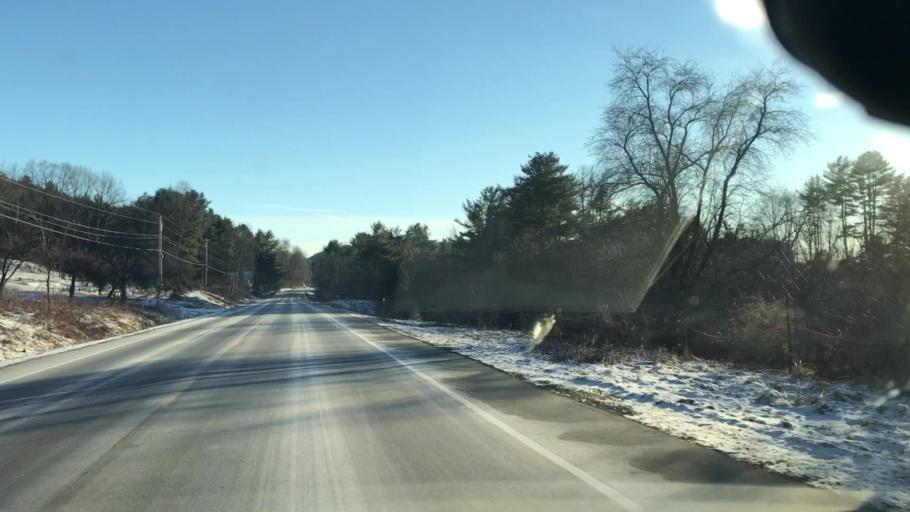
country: US
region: New Hampshire
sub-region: Grafton County
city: Lyme Town Offices
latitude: 43.8599
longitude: -72.1553
